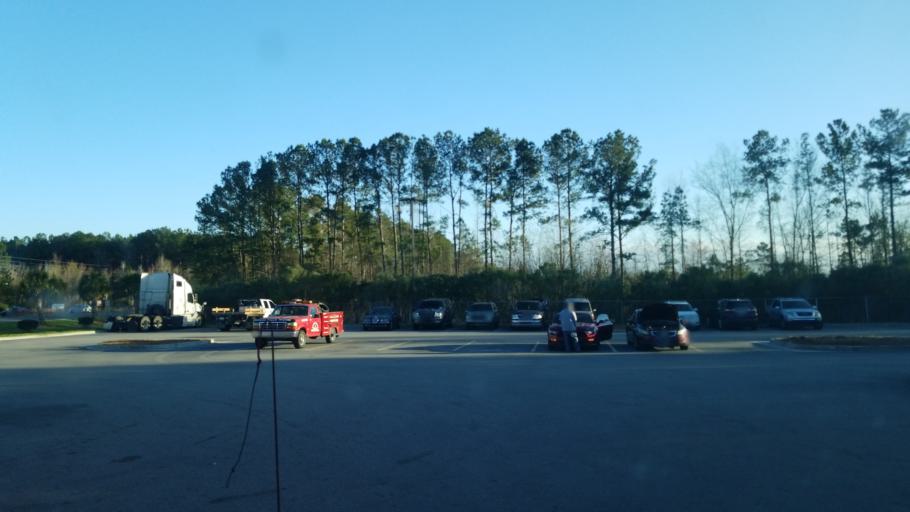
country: US
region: South Carolina
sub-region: Jasper County
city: Hardeeville
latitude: 32.2688
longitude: -81.0808
